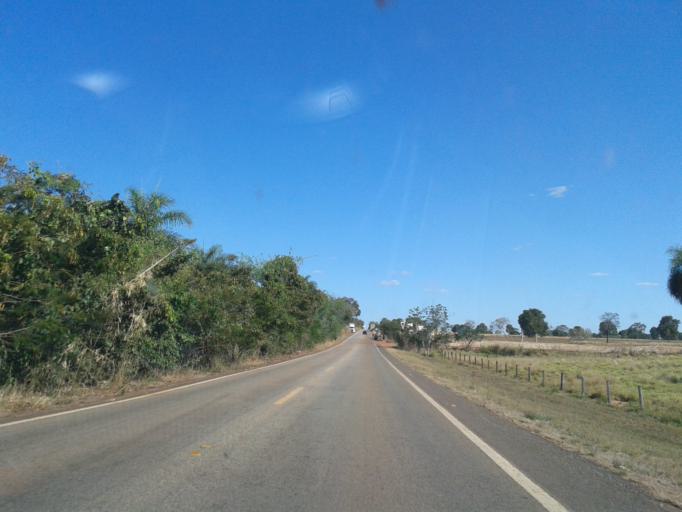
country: BR
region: Goias
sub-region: Mozarlandia
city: Mozarlandia
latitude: -14.2741
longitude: -50.4001
